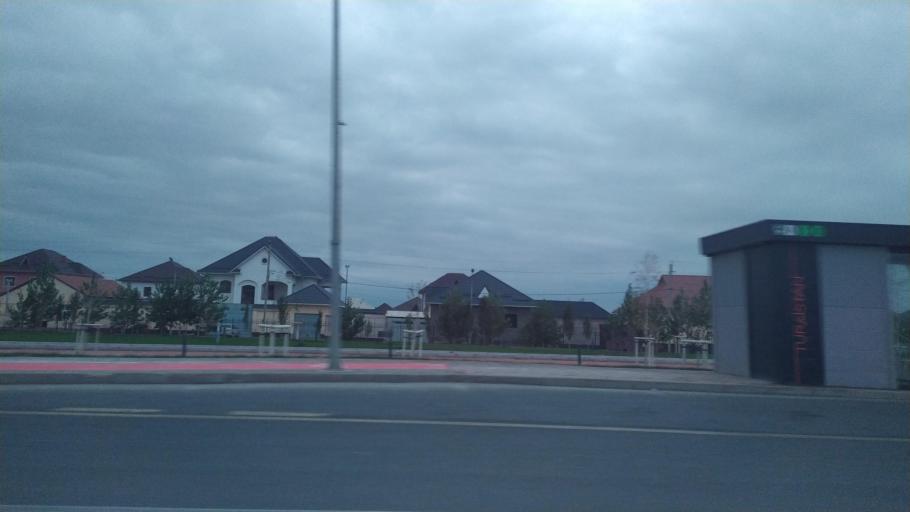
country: KZ
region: Ongtustik Qazaqstan
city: Turkestan
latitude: 43.2786
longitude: 68.3262
